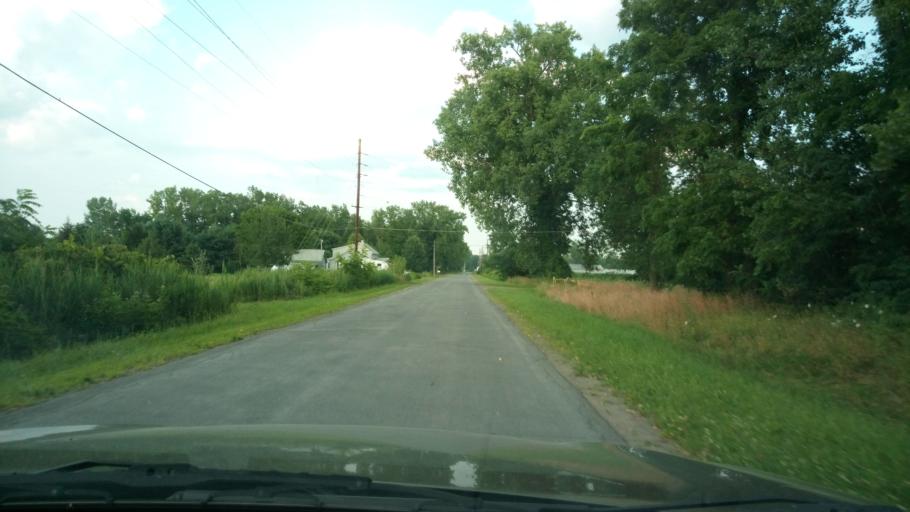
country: US
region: New York
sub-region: Wayne County
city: Clyde
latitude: 43.0887
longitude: -76.9027
